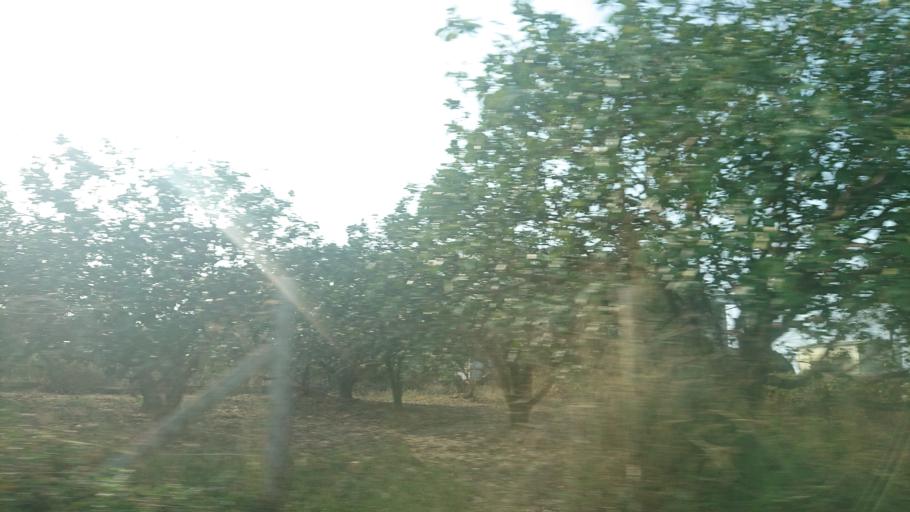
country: TW
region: Taiwan
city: Xinying
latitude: 23.1957
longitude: 120.2717
